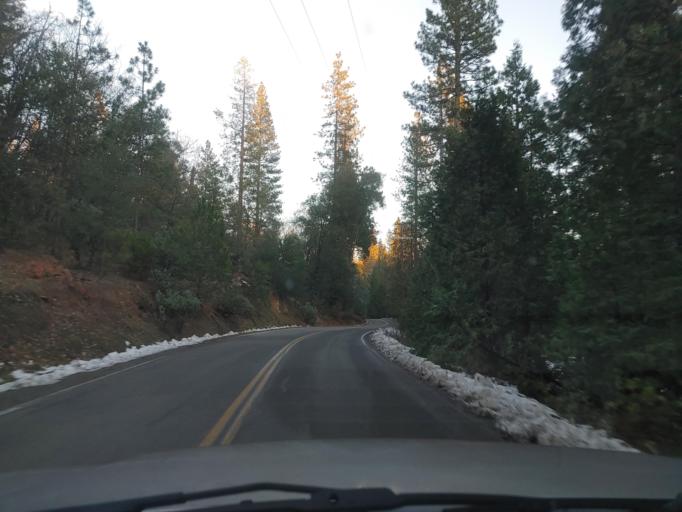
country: US
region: California
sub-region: Tuolumne County
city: Cedar Ridge
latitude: 38.0327
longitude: -120.2695
